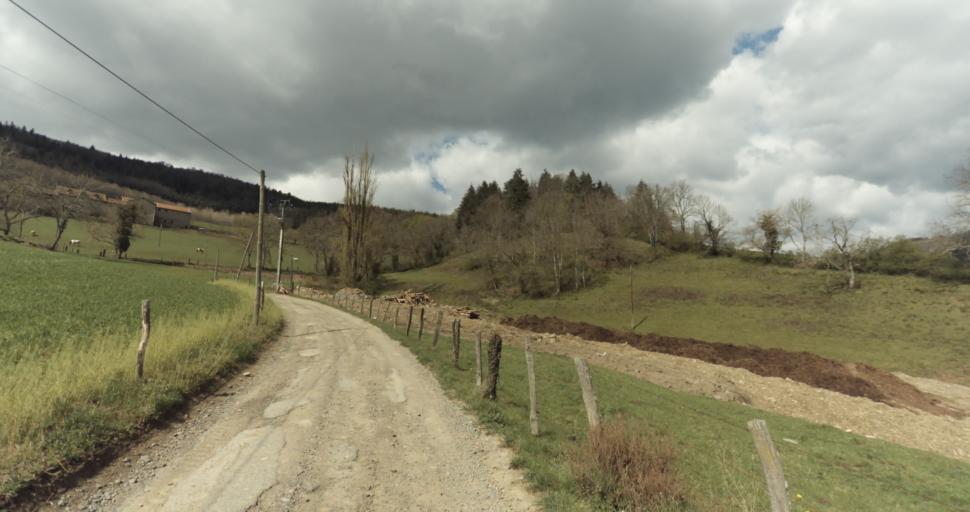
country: FR
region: Rhone-Alpes
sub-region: Departement du Rhone
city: Tarare
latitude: 45.9146
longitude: 4.4154
